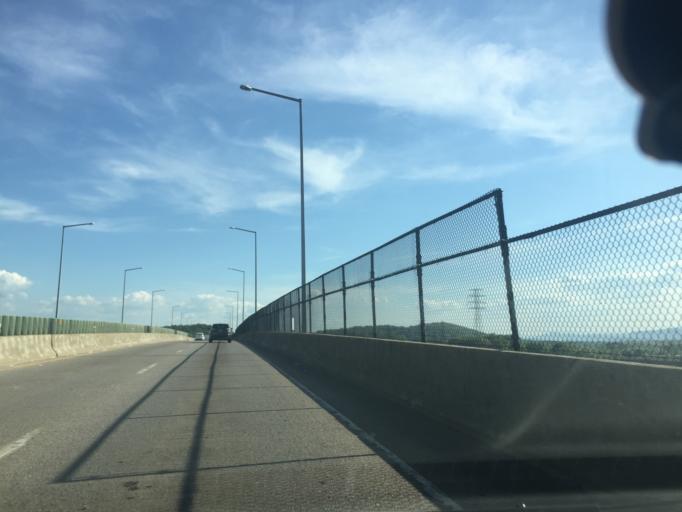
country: US
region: Tennessee
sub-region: Hamilton County
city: East Chattanooga
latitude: 35.1074
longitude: -85.2293
